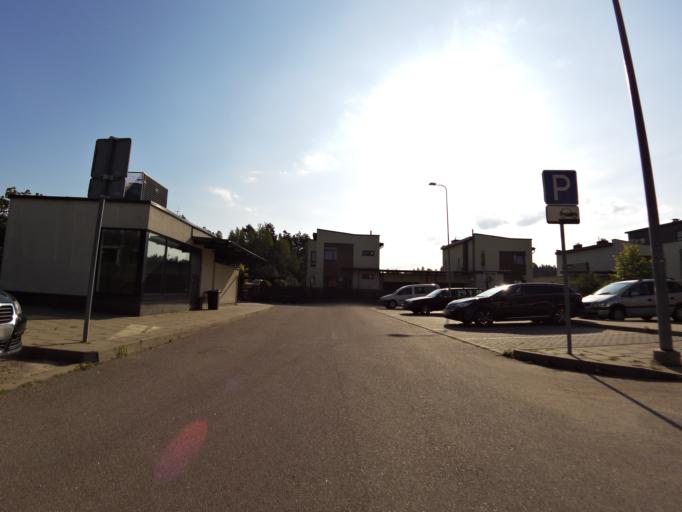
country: LT
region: Vilnius County
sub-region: Vilnius
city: Fabijoniskes
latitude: 54.7632
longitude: 25.2859
